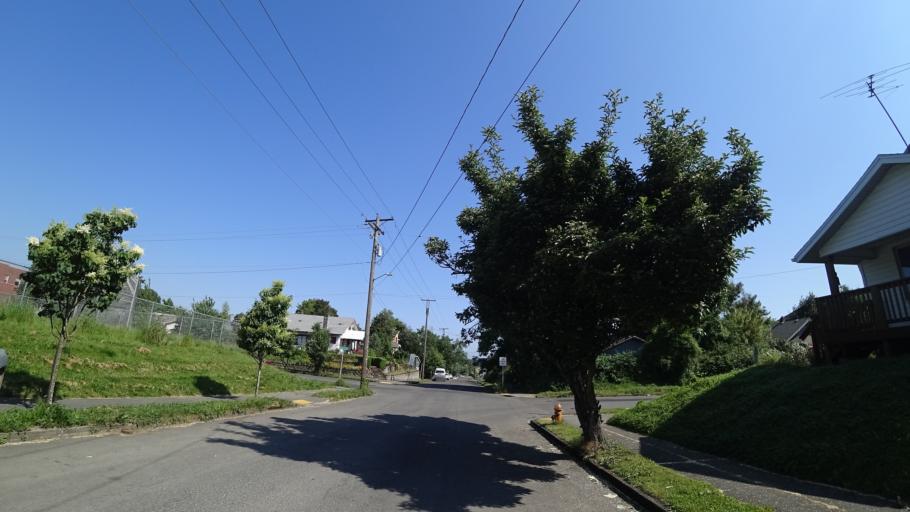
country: US
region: Oregon
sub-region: Multnomah County
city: Portland
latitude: 45.5747
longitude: -122.6517
